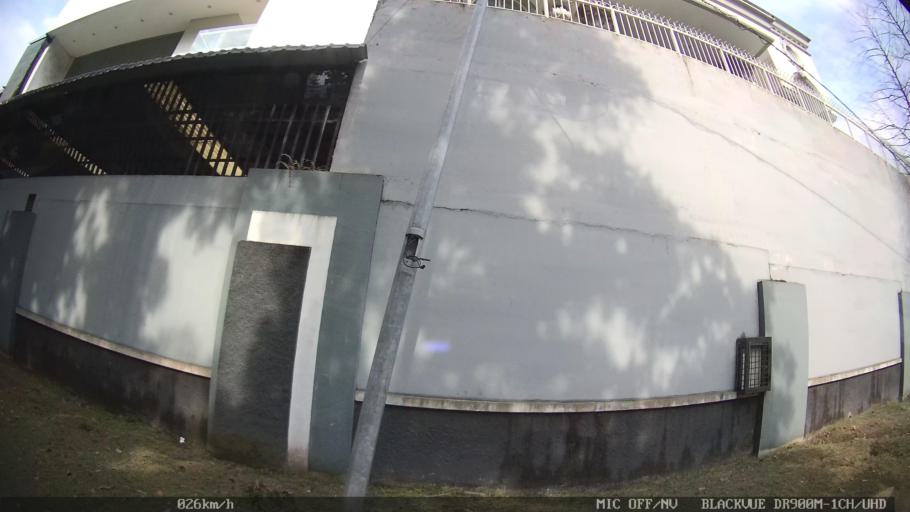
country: ID
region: North Sumatra
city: Medan
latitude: 3.5642
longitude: 98.6837
